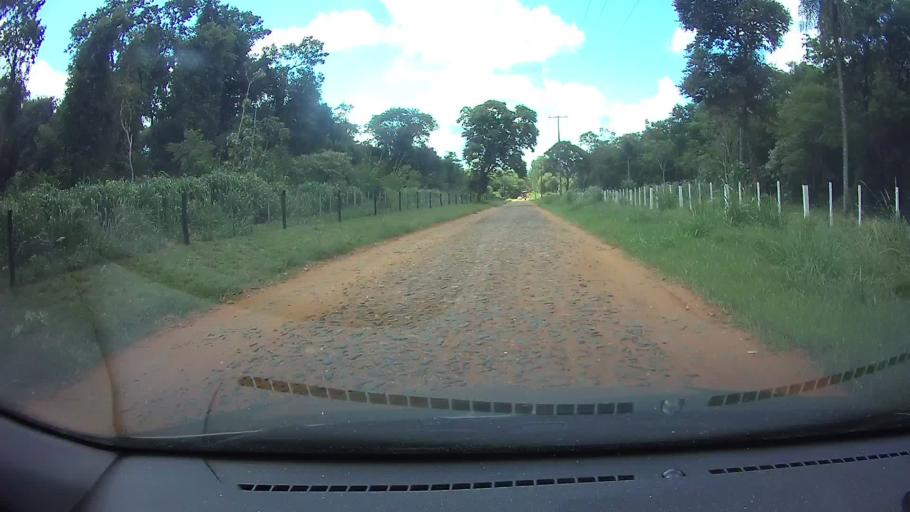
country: PY
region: Paraguari
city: La Colmena
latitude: -25.9200
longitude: -56.7941
